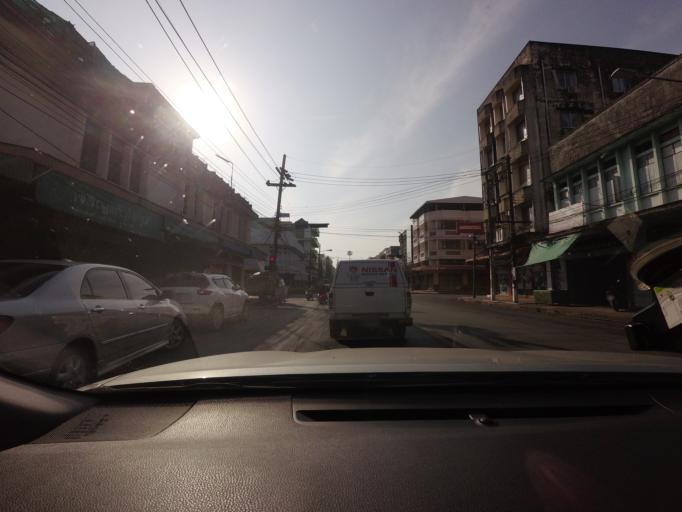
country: TH
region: Yala
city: Yala
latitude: 6.5575
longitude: 101.2894
